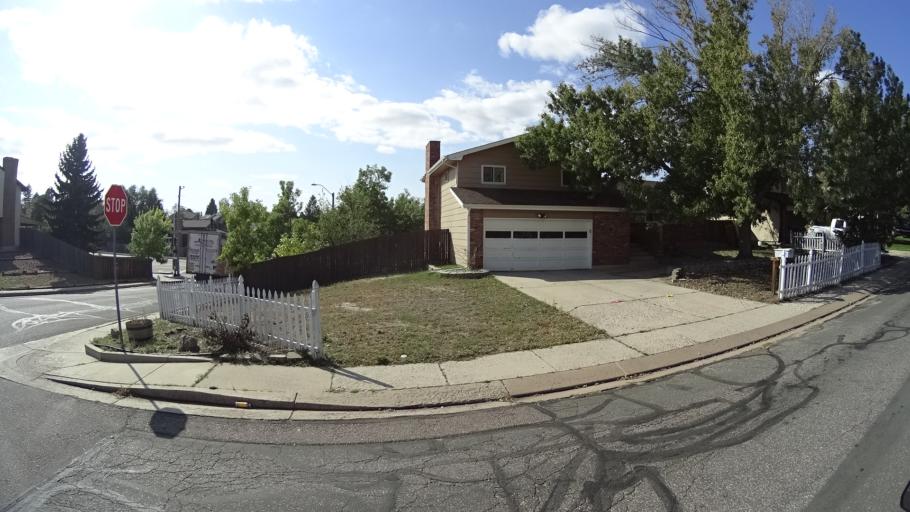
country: US
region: Colorado
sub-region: El Paso County
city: Cimarron Hills
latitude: 38.8855
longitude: -104.7301
